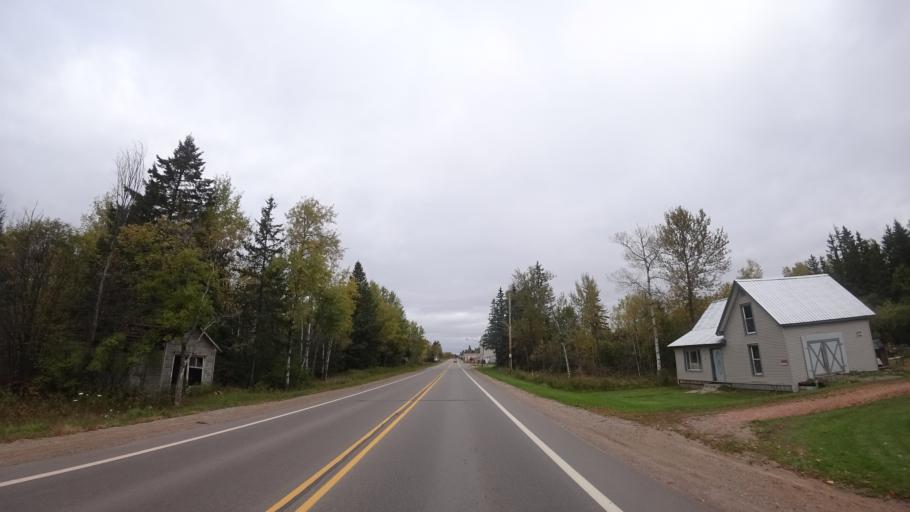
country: US
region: Michigan
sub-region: Iron County
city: Crystal Falls
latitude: 46.1371
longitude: -88.0932
